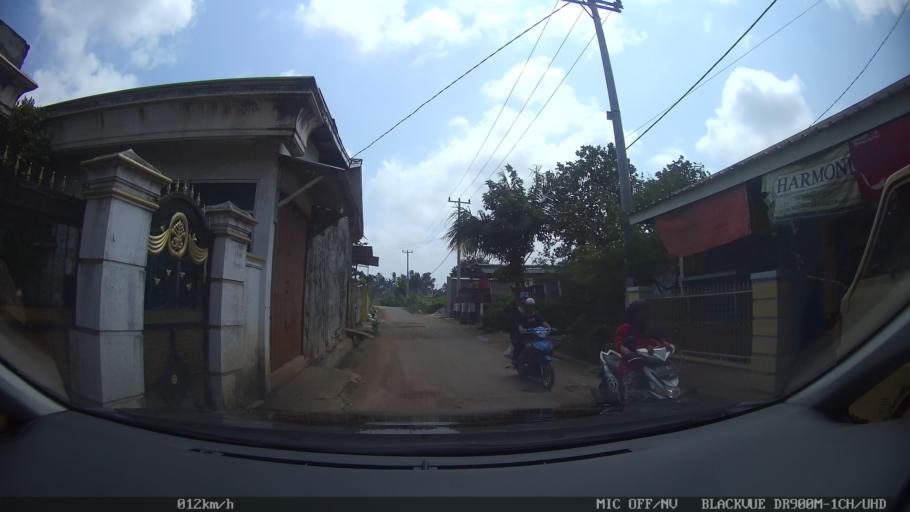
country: ID
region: Lampung
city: Kedaton
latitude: -5.3535
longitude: 105.2872
